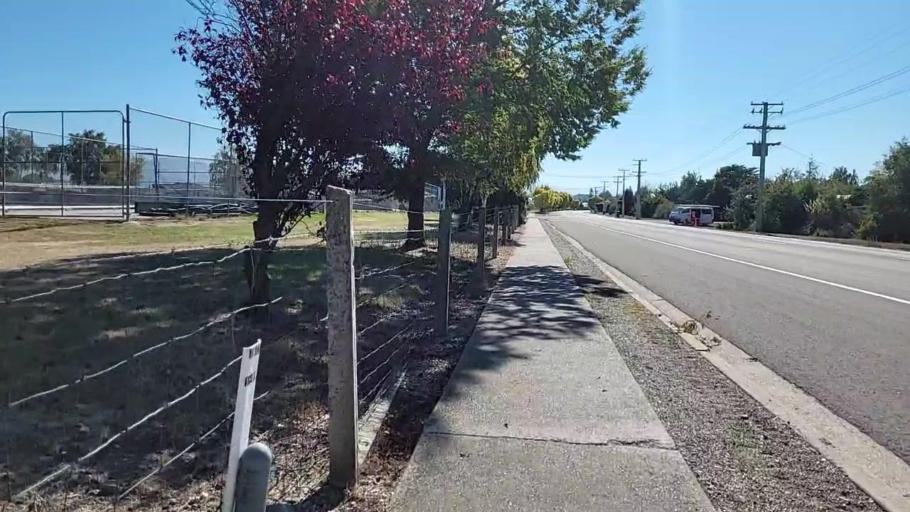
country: NZ
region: Otago
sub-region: Queenstown-Lakes District
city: Wanaka
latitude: -45.1005
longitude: 169.5967
